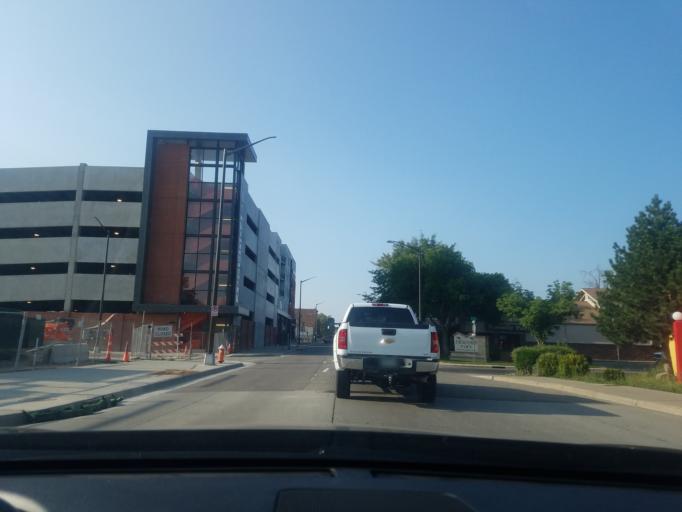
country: US
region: Colorado
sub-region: Larimer County
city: Loveland
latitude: 40.3931
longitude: -105.0732
